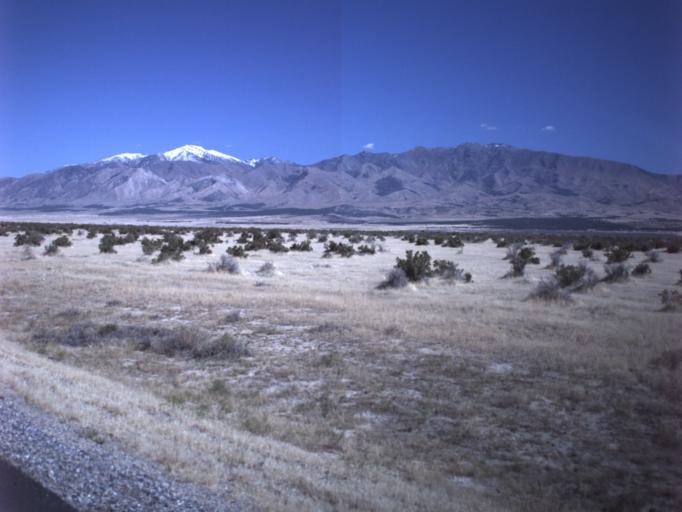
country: US
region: Utah
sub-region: Tooele County
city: Grantsville
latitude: 40.2774
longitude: -112.7416
